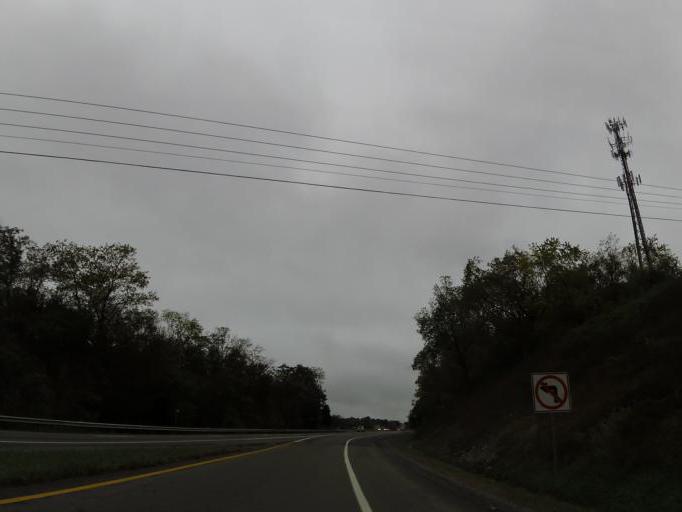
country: US
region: Virginia
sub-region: Wythe County
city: Wytheville
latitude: 36.9626
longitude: -81.0680
